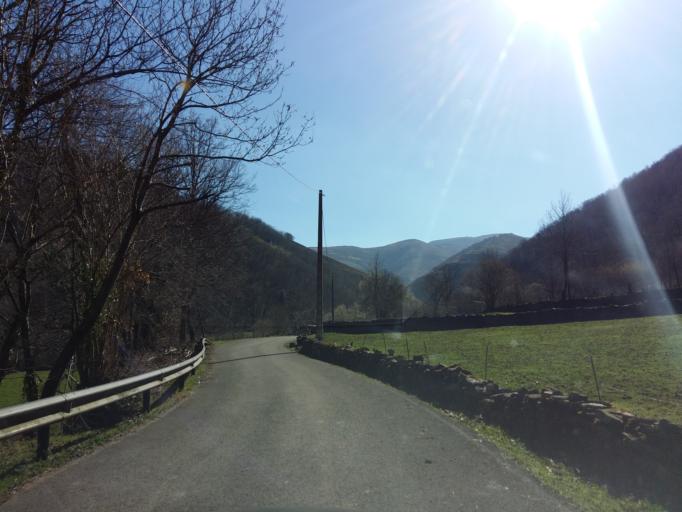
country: ES
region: Cantabria
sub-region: Provincia de Cantabria
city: Vega de Pas
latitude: 43.1392
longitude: -3.7943
